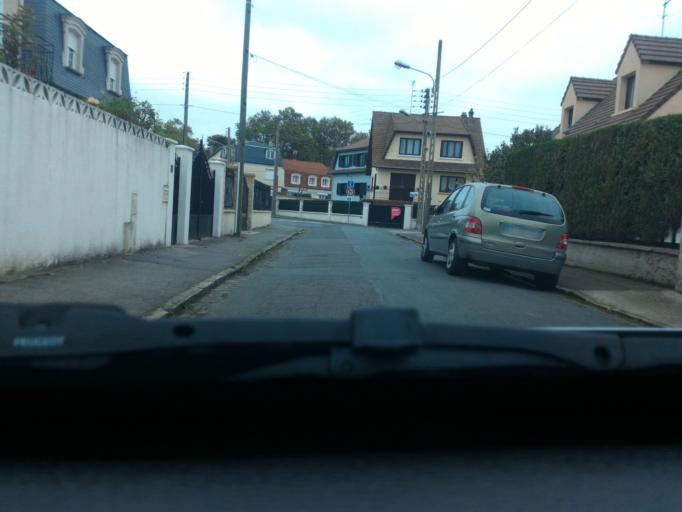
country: FR
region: Ile-de-France
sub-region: Departement du Val-de-Marne
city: Chennevieres-sur-Marne
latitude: 48.8024
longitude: 2.5444
